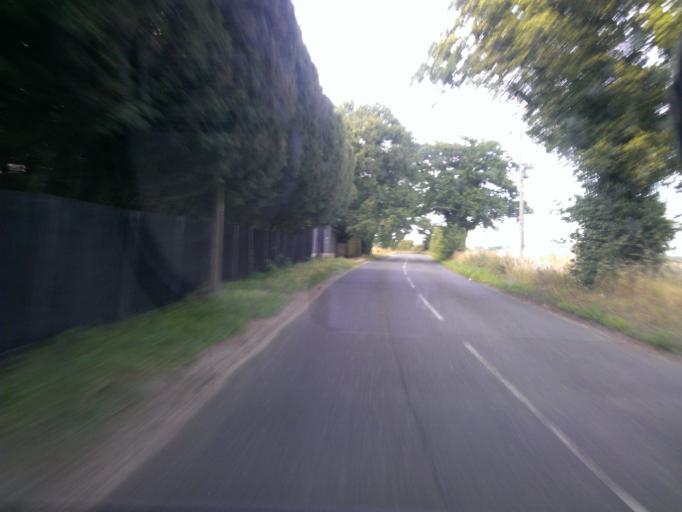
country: GB
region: England
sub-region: Essex
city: Great Bentley
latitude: 51.8632
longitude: 1.0670
